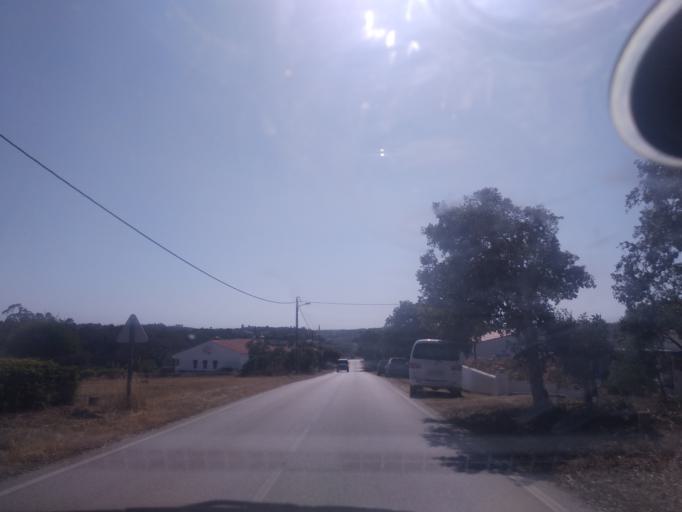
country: PT
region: Faro
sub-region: Aljezur
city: Aljezur
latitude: 37.2275
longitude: -8.8180
